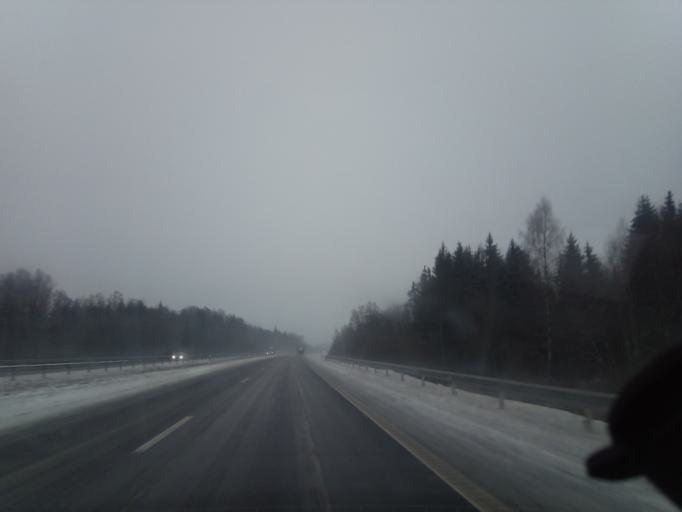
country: LT
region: Vilnius County
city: Pasilaiciai
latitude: 54.8449
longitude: 25.1096
